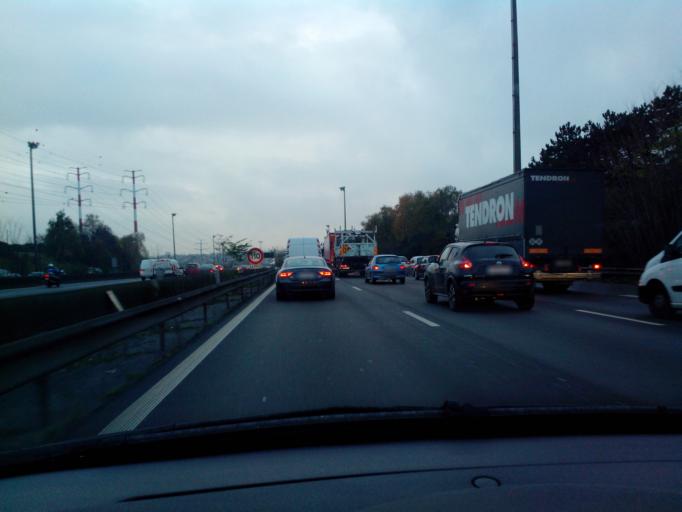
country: FR
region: Ile-de-France
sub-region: Departement du Val-de-Marne
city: Fresnes
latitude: 48.7520
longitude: 2.3301
